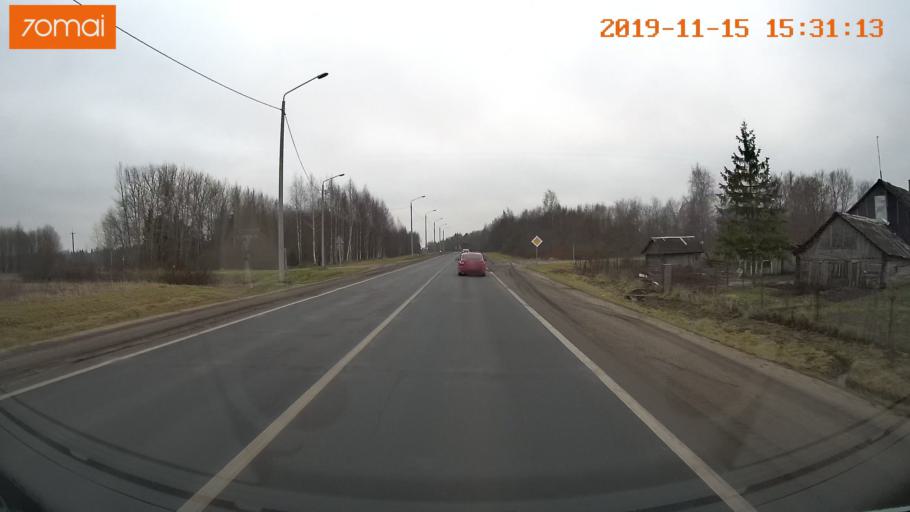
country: RU
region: Jaroslavl
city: Danilov
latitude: 58.1024
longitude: 40.1089
